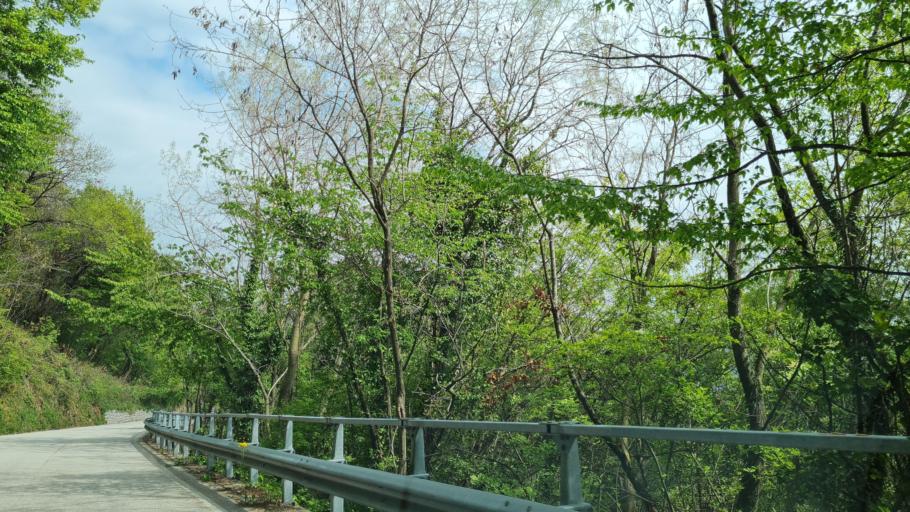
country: IT
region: Veneto
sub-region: Provincia di Vicenza
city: Marostica
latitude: 45.7814
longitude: 11.6716
